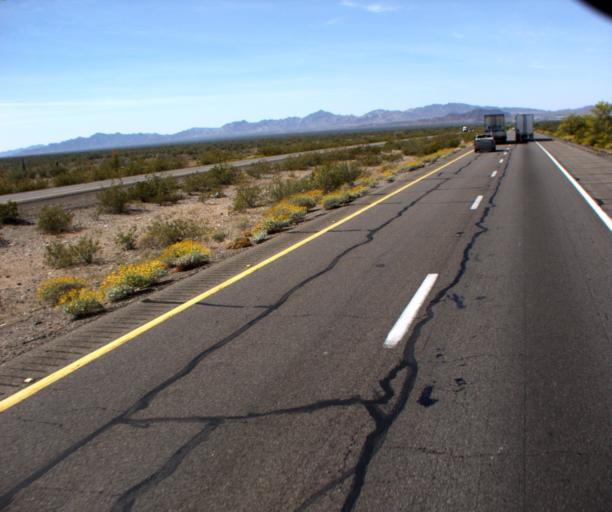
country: US
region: Arizona
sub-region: La Paz County
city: Quartzsite
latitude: 33.6762
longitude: -114.1255
